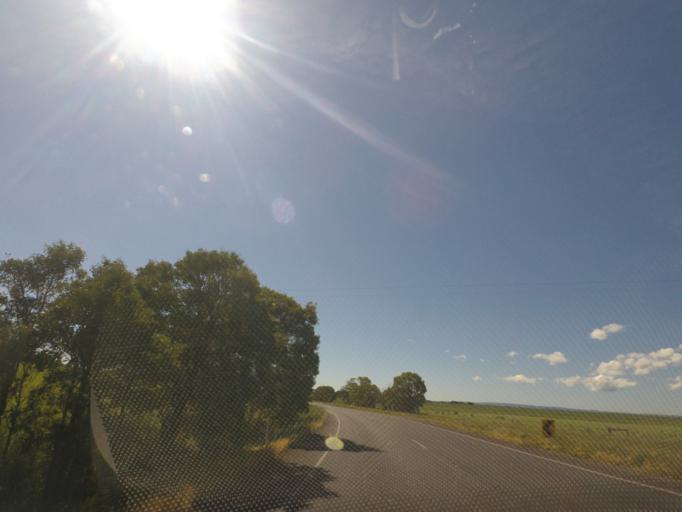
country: AU
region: Victoria
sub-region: Moorabool
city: Bacchus Marsh
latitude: -37.7406
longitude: 144.2223
